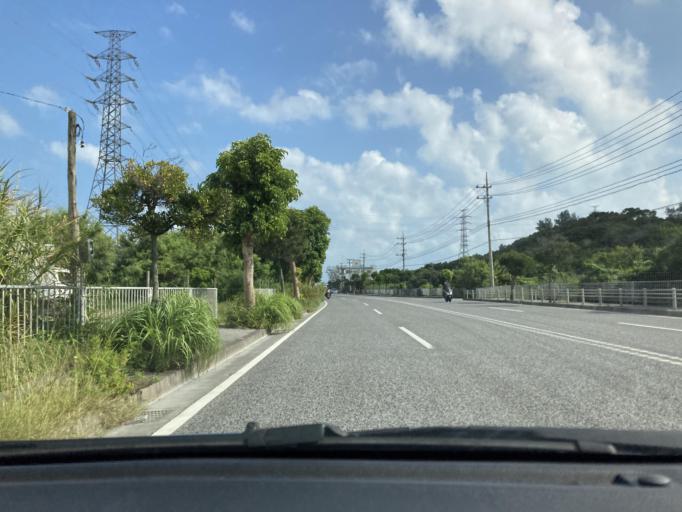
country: JP
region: Okinawa
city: Chatan
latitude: 26.2920
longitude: 127.8107
